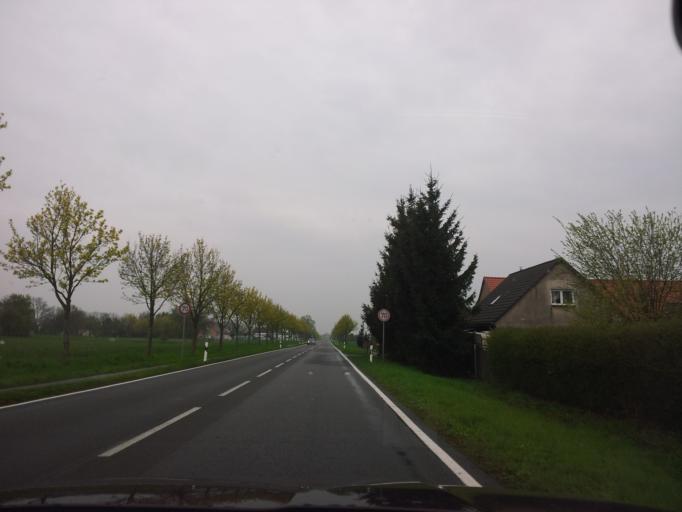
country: DE
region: Saxony-Anhalt
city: Kropstadt
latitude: 52.0172
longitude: 12.7914
